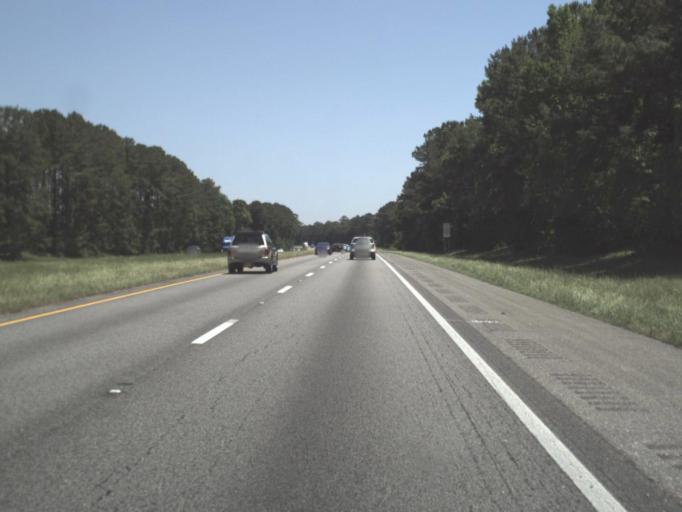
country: US
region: Florida
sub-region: Jefferson County
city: Monticello
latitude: 30.4497
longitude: -83.7504
